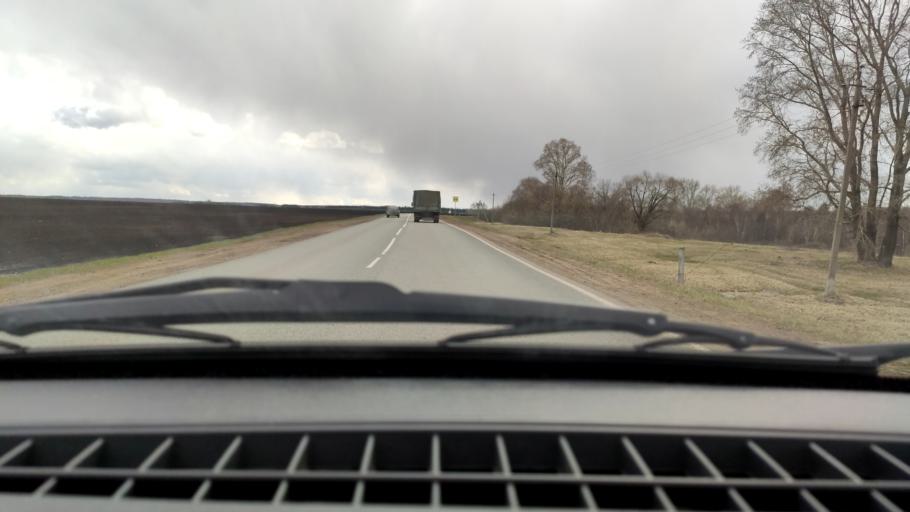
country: RU
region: Bashkortostan
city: Kushnarenkovo
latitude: 55.0701
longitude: 55.2600
